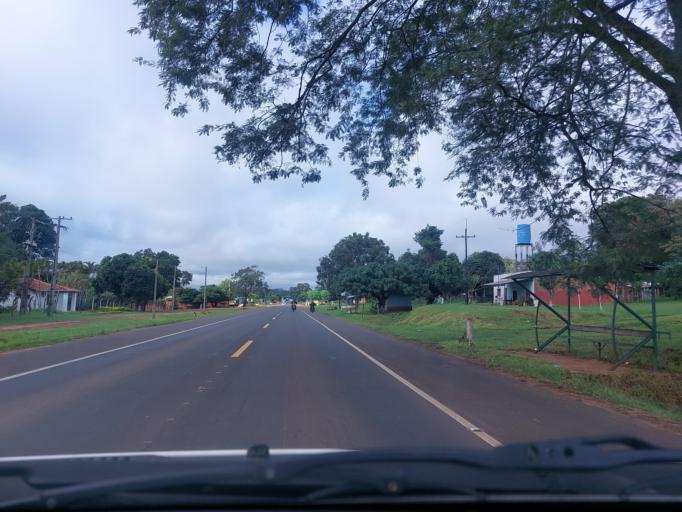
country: PY
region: San Pedro
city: Guayaybi
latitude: -24.5762
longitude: -56.4025
